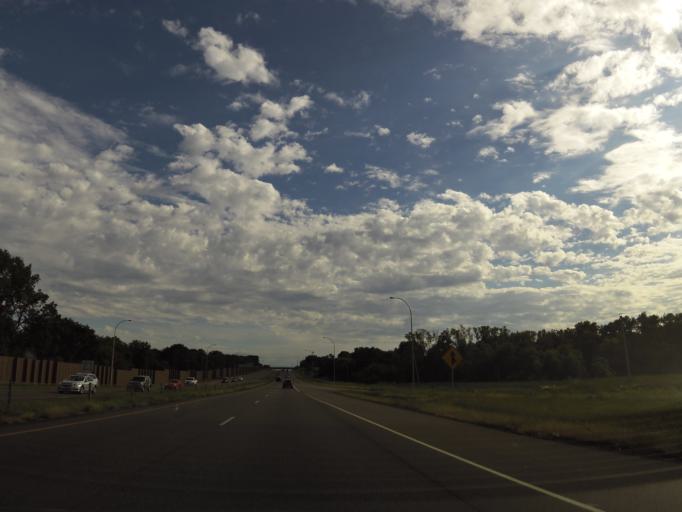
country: US
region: Minnesota
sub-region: Hennepin County
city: New Hope
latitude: 45.0312
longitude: -93.4010
